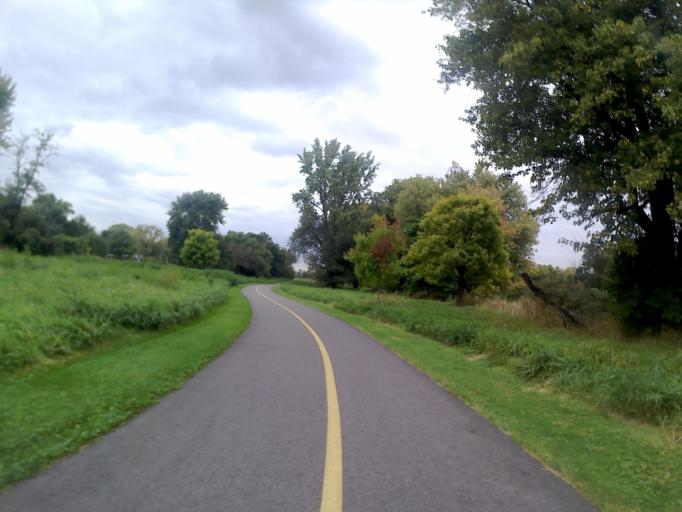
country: US
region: Illinois
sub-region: Kane County
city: Montgomery
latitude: 41.7351
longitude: -88.3318
